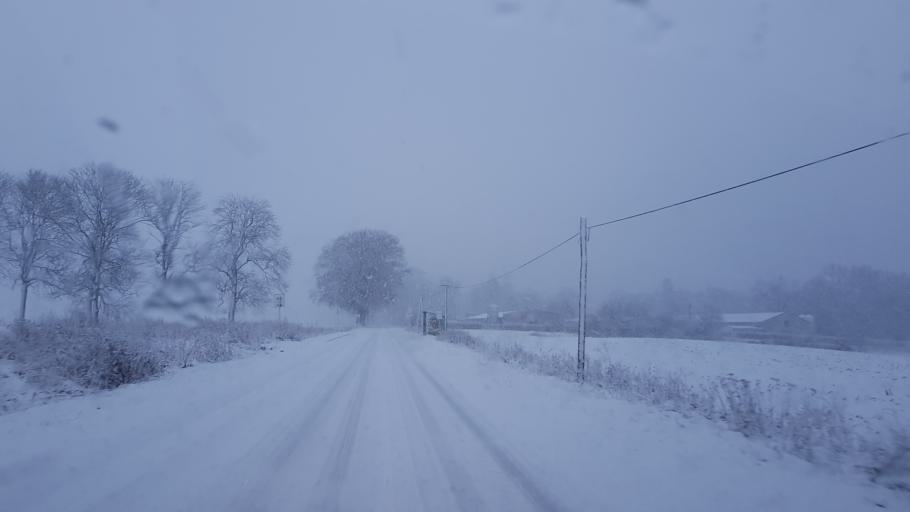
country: PL
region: West Pomeranian Voivodeship
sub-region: Powiat koszalinski
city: Polanow
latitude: 54.1881
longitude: 16.5169
